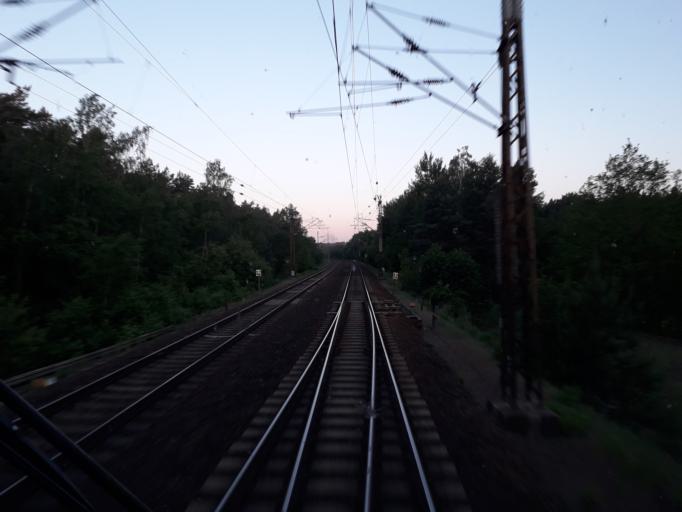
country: DE
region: Brandenburg
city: Hennigsdorf
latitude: 52.6582
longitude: 13.1921
